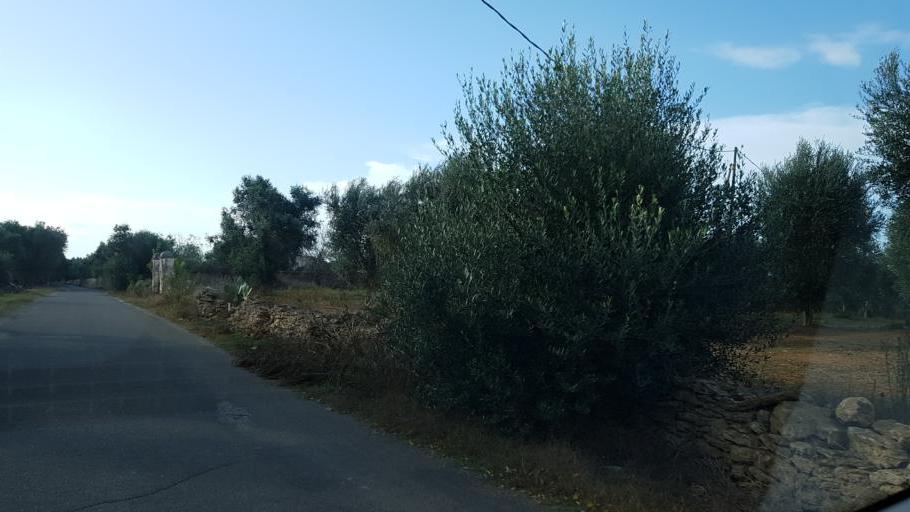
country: IT
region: Apulia
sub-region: Provincia di Brindisi
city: Oria
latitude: 40.5098
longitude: 17.6708
